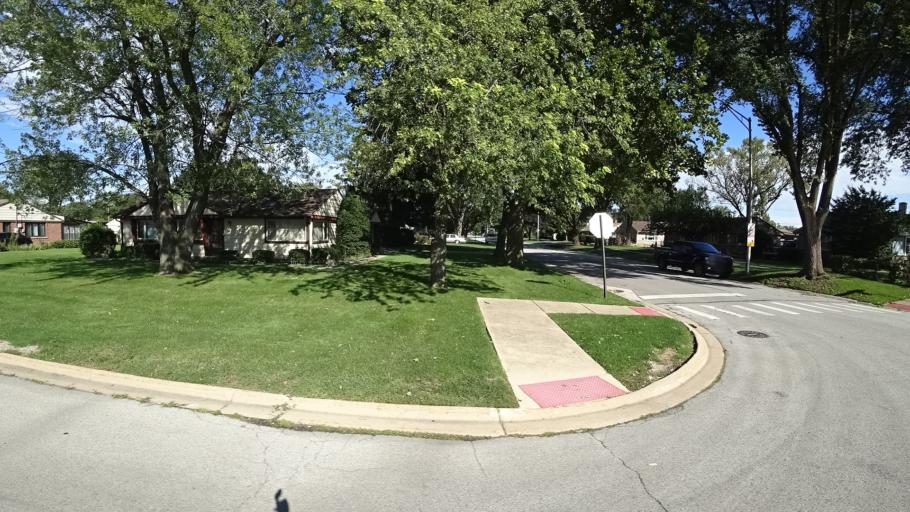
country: US
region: Illinois
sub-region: Cook County
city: Oak Lawn
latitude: 41.7087
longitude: -87.7501
